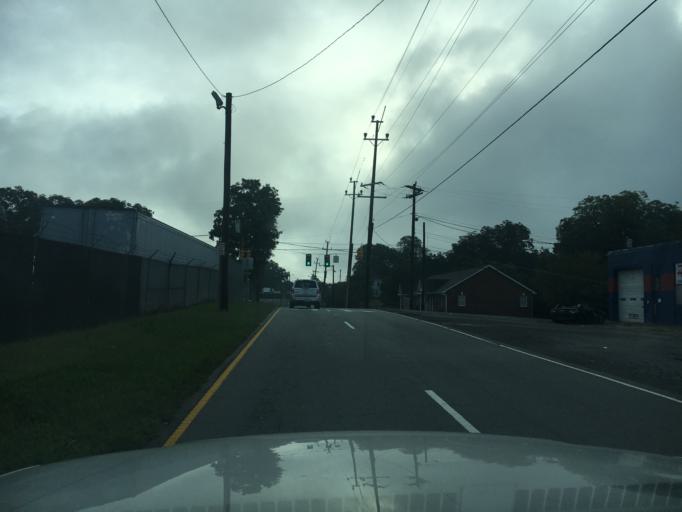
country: US
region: North Carolina
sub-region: Catawba County
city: Hickory
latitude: 35.7300
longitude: -81.3535
